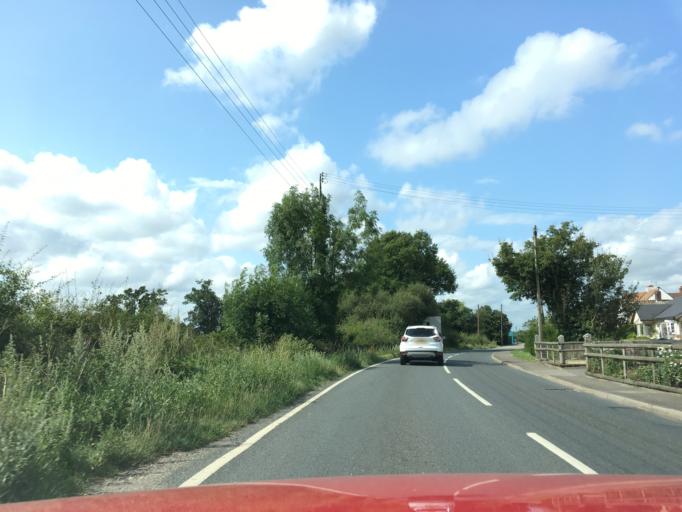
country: GB
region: England
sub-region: Kent
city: Headcorn
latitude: 51.1255
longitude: 0.6476
